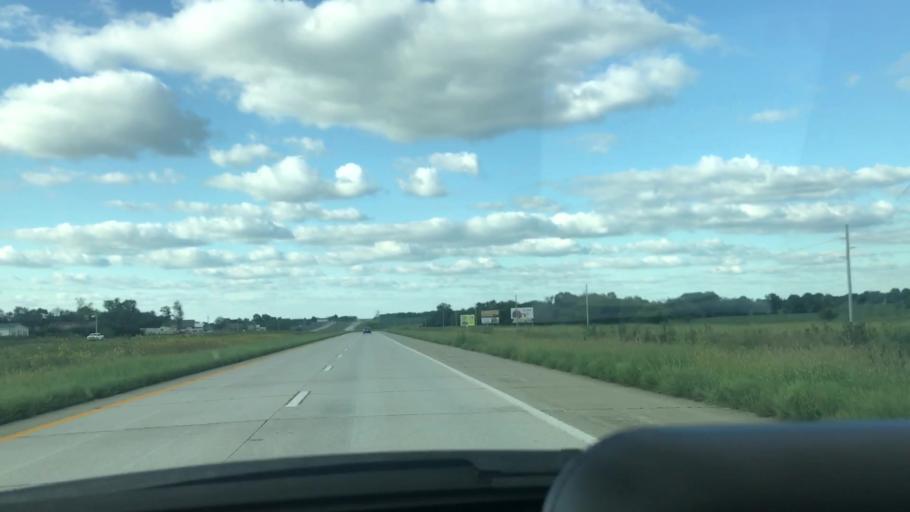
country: US
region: Missouri
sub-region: Benton County
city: Cole Camp
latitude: 38.5184
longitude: -93.2723
